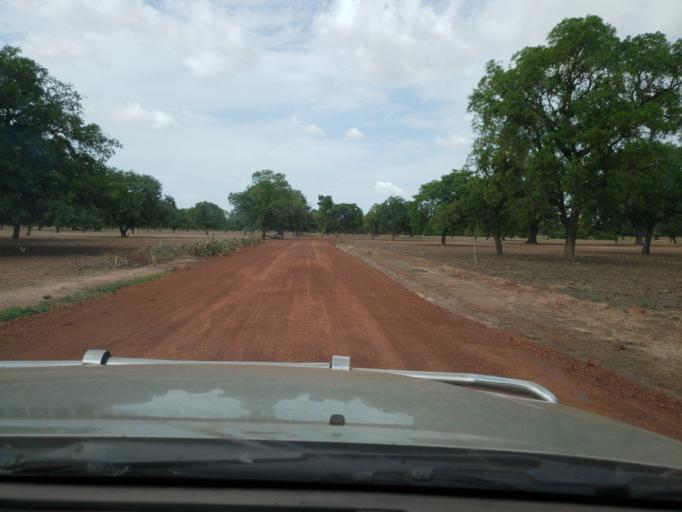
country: ML
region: Segou
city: Bla
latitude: 12.7203
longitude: -5.6797
